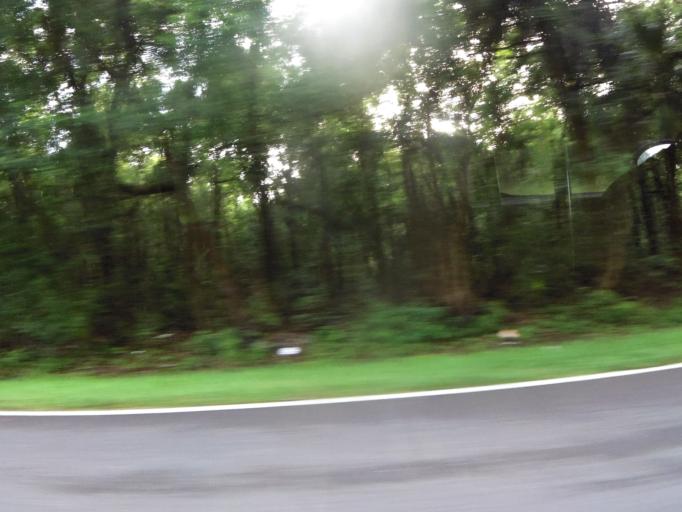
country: US
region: Florida
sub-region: Nassau County
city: Nassau Village-Ratliff
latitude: 30.4116
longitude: -81.7752
